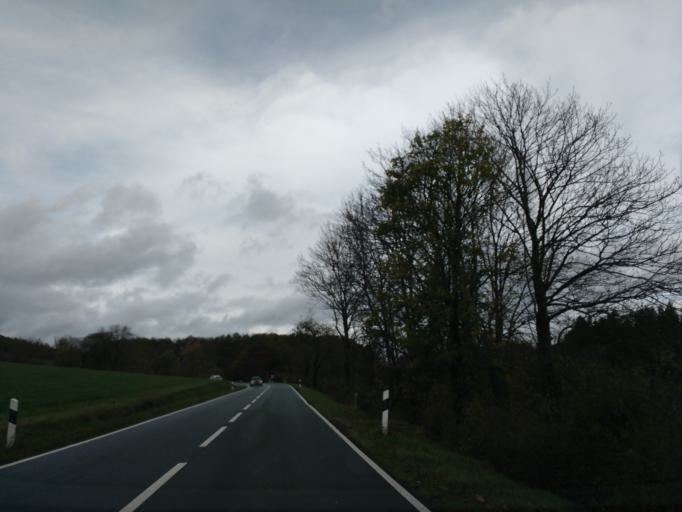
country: DE
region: Hesse
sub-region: Regierungsbezirk Kassel
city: Vohl
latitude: 51.1878
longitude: 8.9045
